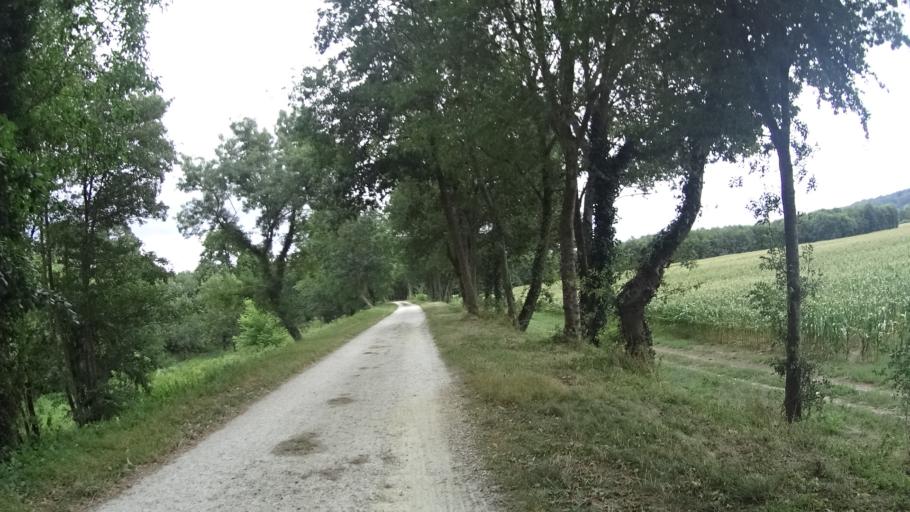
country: FR
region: Centre
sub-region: Departement d'Indre-et-Loire
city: Huismes
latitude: 47.2490
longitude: 0.2463
